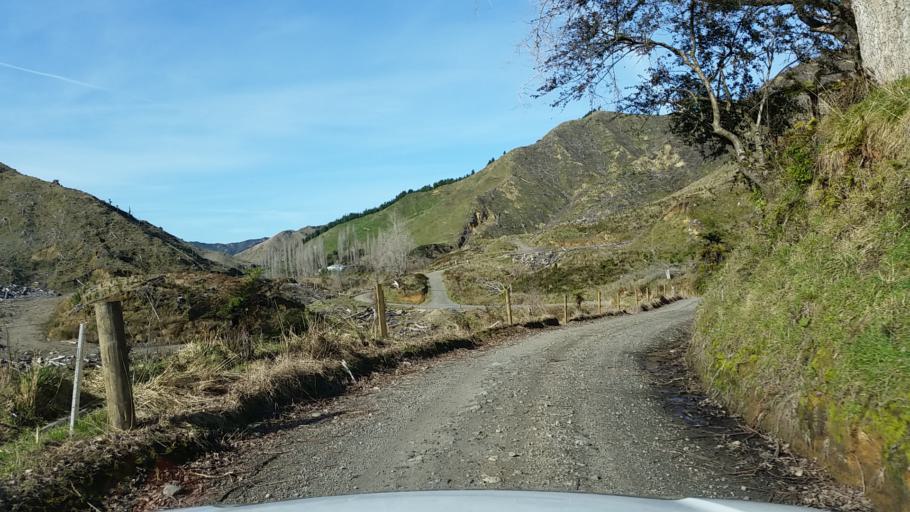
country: NZ
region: Taranaki
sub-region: South Taranaki District
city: Eltham
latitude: -39.3620
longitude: 174.5150
